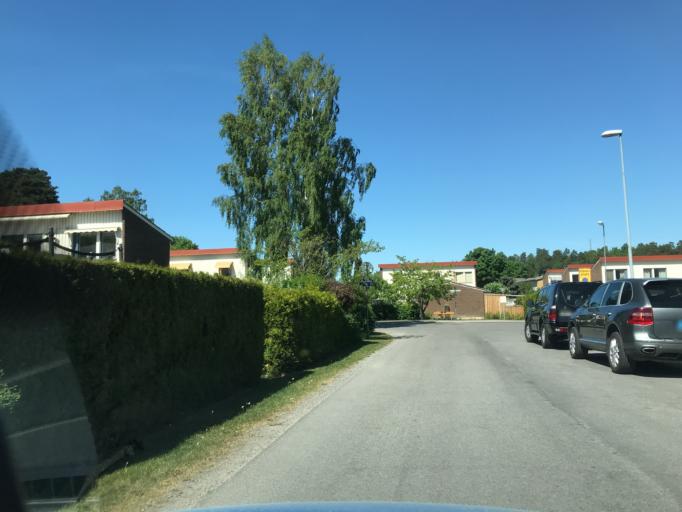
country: SE
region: Stockholm
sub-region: Stockholms Kommun
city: Kista
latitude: 59.4065
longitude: 17.9783
